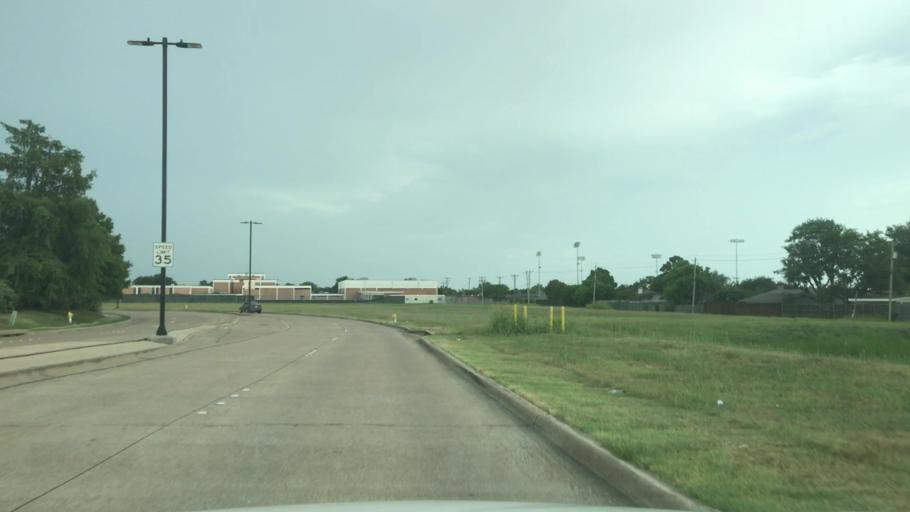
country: US
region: Texas
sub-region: Dallas County
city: Garland
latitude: 32.8757
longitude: -96.6220
